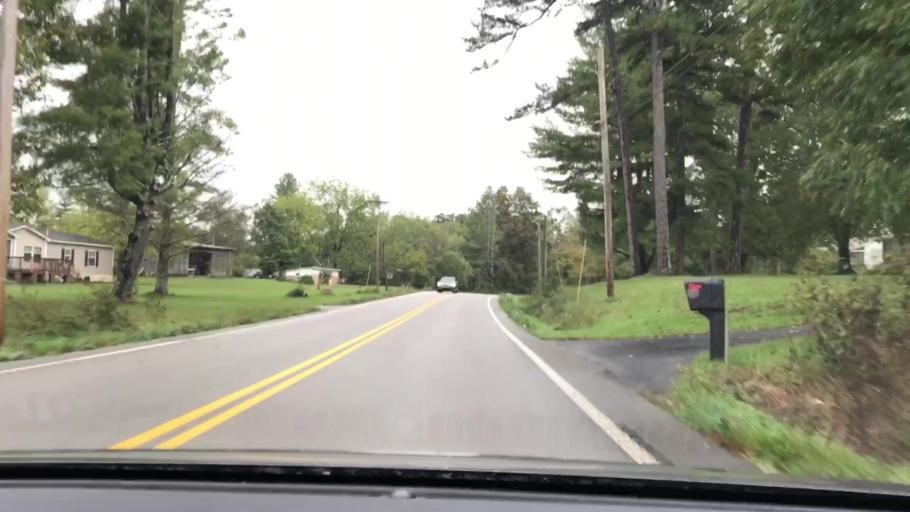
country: US
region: Tennessee
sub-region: Fentress County
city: Jamestown
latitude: 36.3745
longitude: -84.7805
